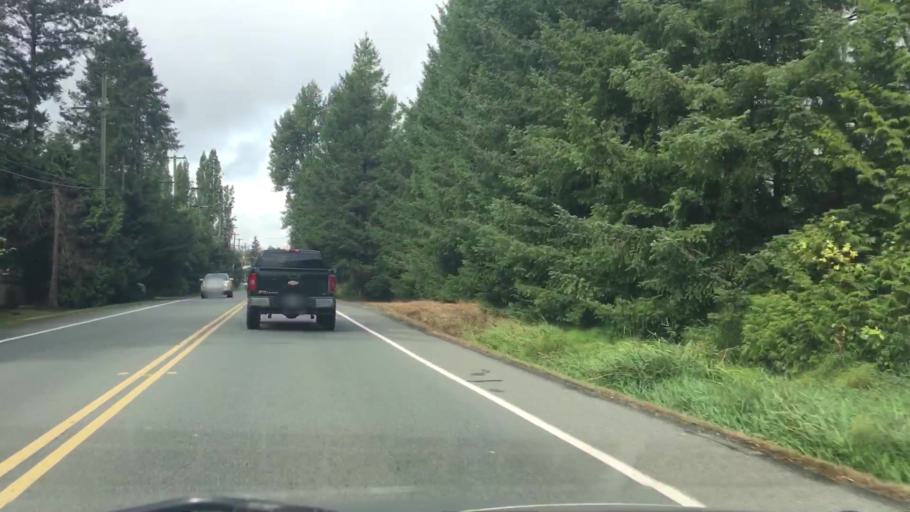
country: CA
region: British Columbia
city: Langley
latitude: 49.1040
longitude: -122.5765
